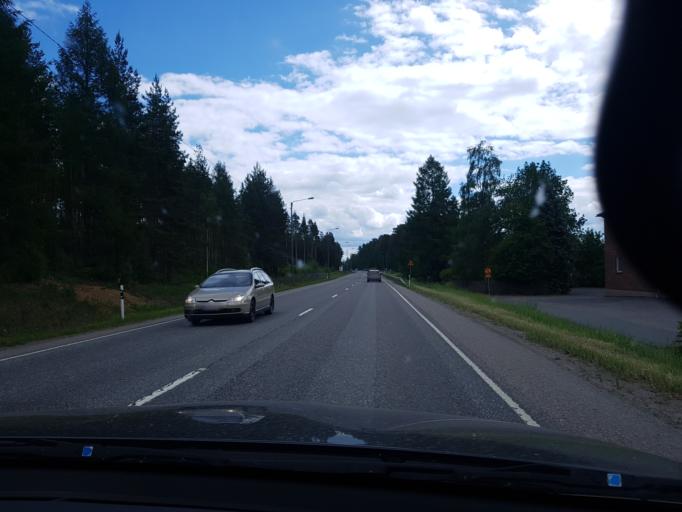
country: FI
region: Pirkanmaa
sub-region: Tampere
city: Paelkaene
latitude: 61.3016
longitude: 24.3022
